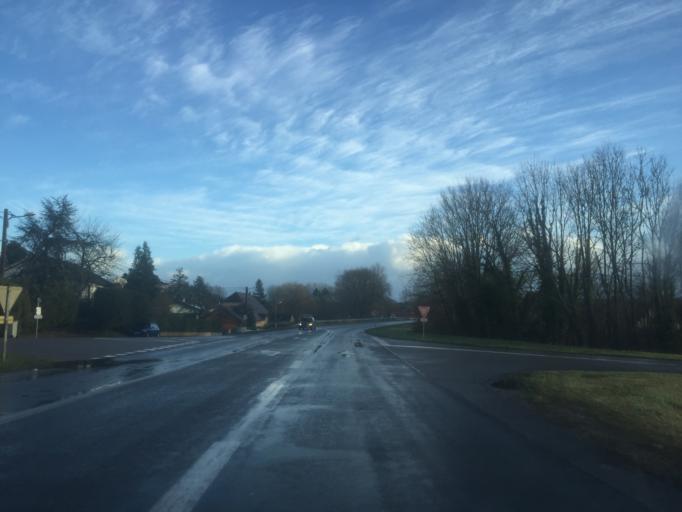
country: FR
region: Franche-Comte
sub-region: Departement du Jura
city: Dampierre
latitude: 47.1499
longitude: 5.7205
